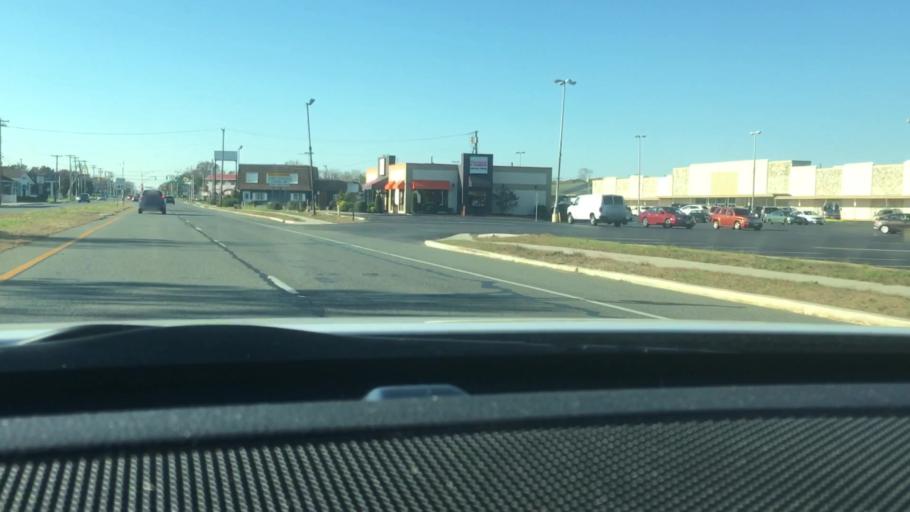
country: US
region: New Jersey
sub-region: Atlantic County
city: Pleasantville
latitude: 39.3937
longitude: -74.5383
